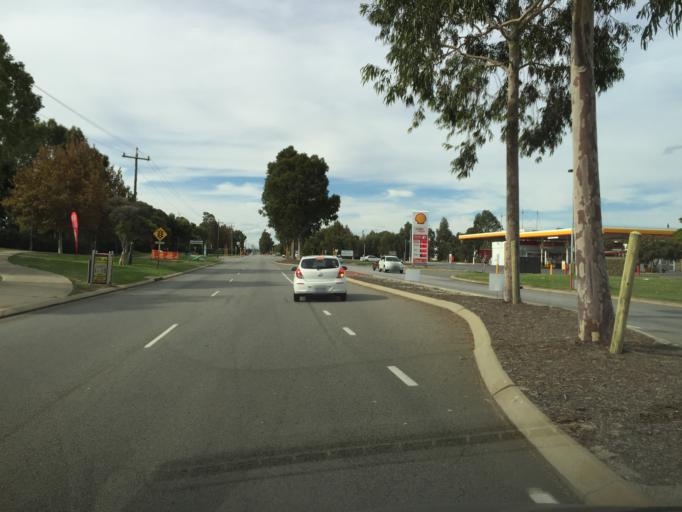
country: AU
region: Western Australia
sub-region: Canning
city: Willetton
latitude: -32.0707
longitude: 115.8945
